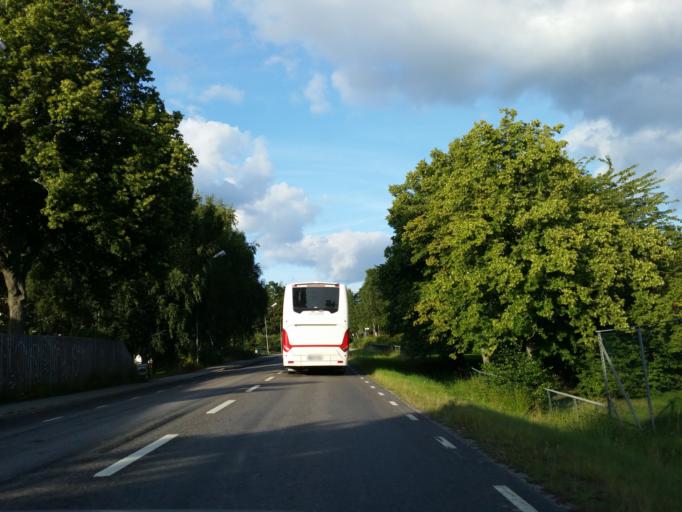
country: SE
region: Stockholm
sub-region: Sodertalje Kommun
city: Pershagen
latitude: 59.0839
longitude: 17.5554
